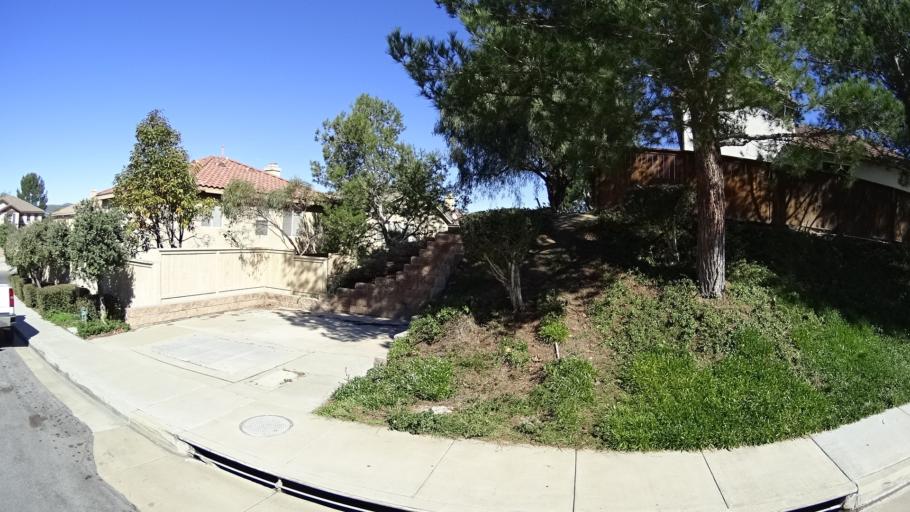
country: US
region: California
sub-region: Orange County
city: Yorba Linda
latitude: 33.8556
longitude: -117.7249
